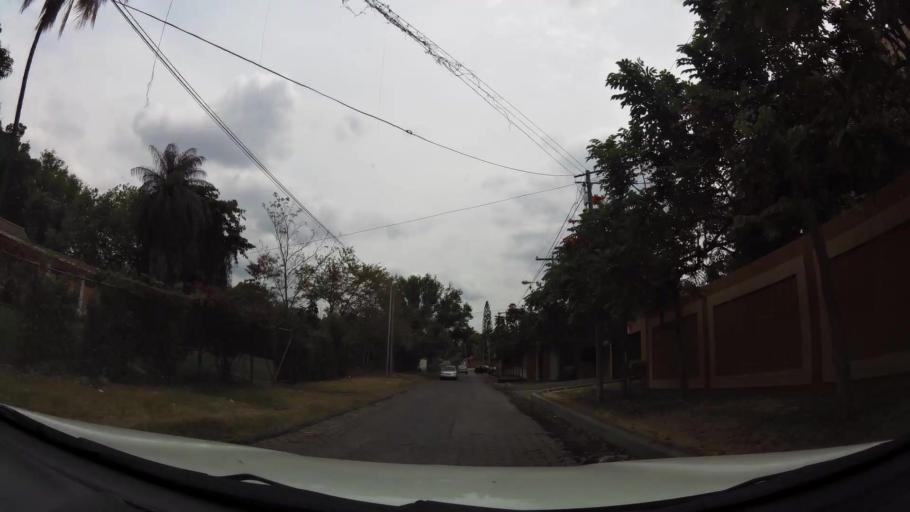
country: NI
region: Managua
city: Managua
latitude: 12.0968
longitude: -86.2294
